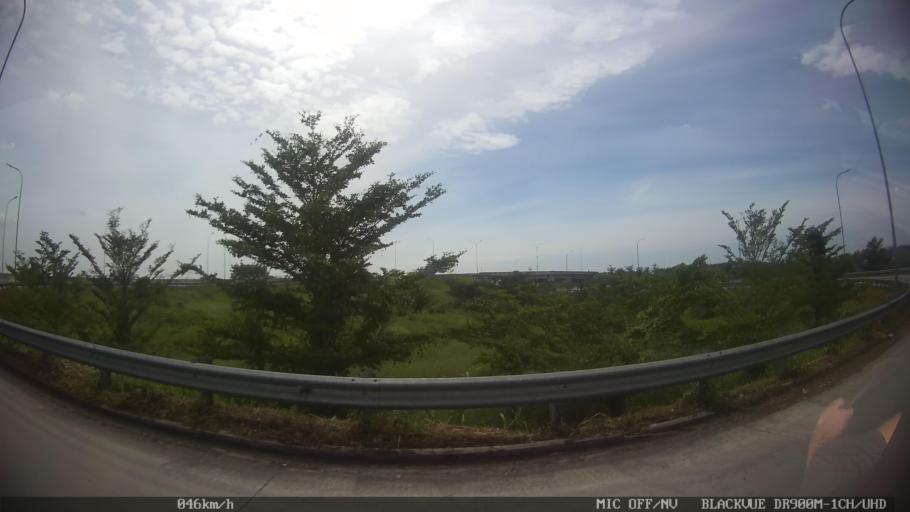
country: ID
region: North Sumatra
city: Medan
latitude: 3.6392
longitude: 98.6356
